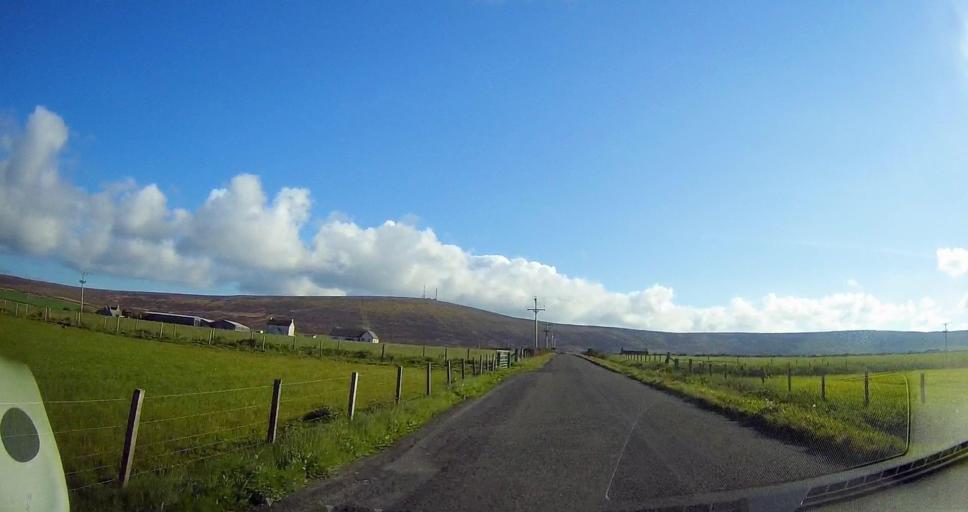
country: GB
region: Scotland
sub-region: Orkney Islands
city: Orkney
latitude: 58.9942
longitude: -3.0706
